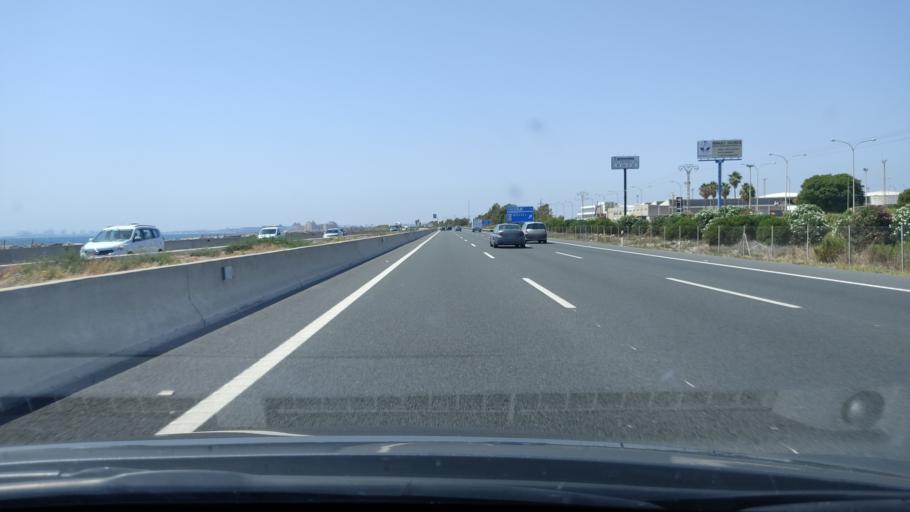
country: ES
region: Valencia
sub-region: Provincia de Valencia
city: Albuixech
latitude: 39.5381
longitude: -0.3059
